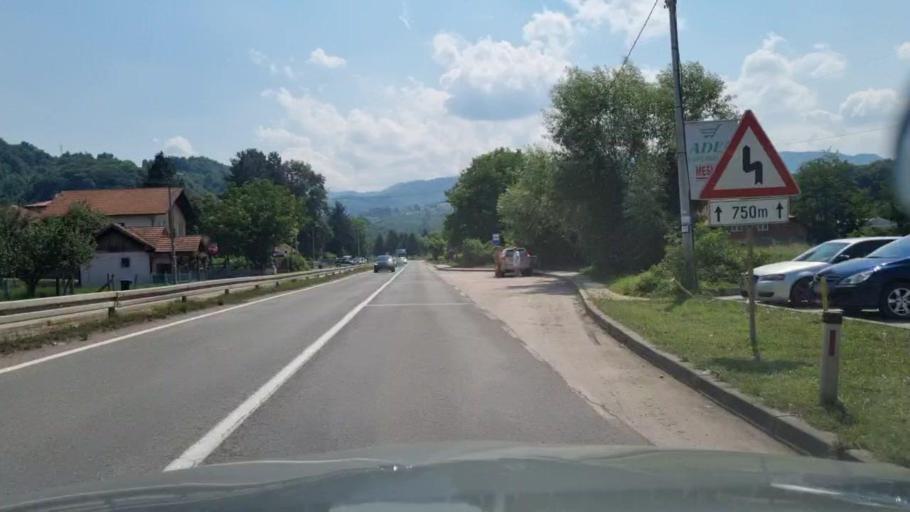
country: BA
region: Federation of Bosnia and Herzegovina
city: Zivinice
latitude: 44.4012
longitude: 18.6640
